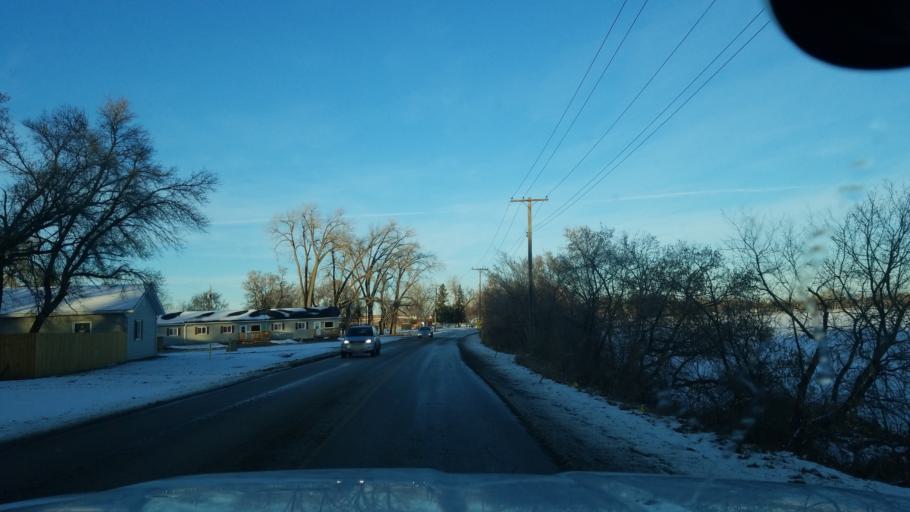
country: CA
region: Manitoba
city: Portage la Prairie
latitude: 49.9635
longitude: -98.3214
